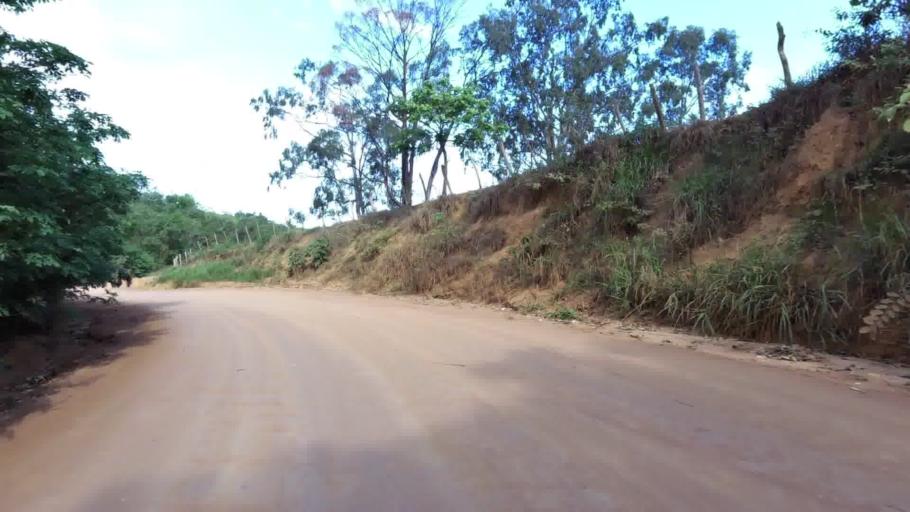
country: BR
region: Espirito Santo
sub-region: Piuma
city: Piuma
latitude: -20.8317
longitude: -40.7403
